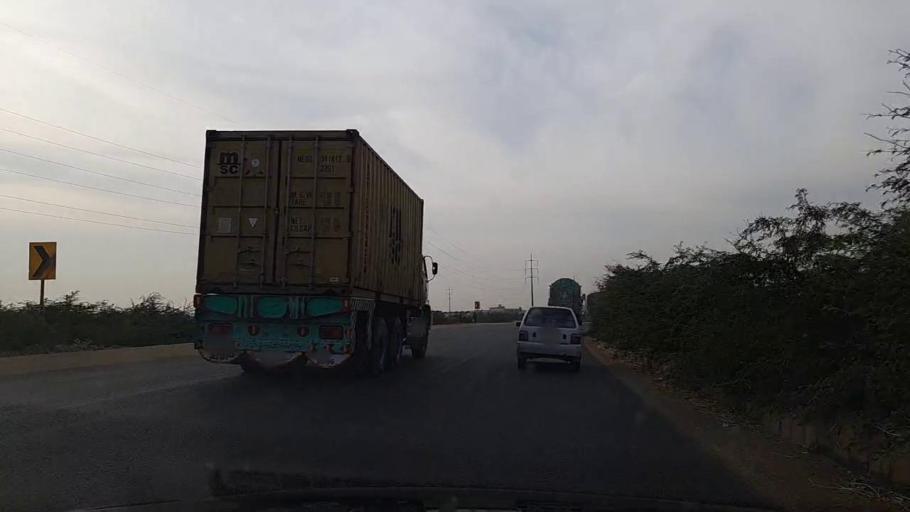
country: PK
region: Sindh
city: Gharo
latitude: 24.8395
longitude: 67.4334
